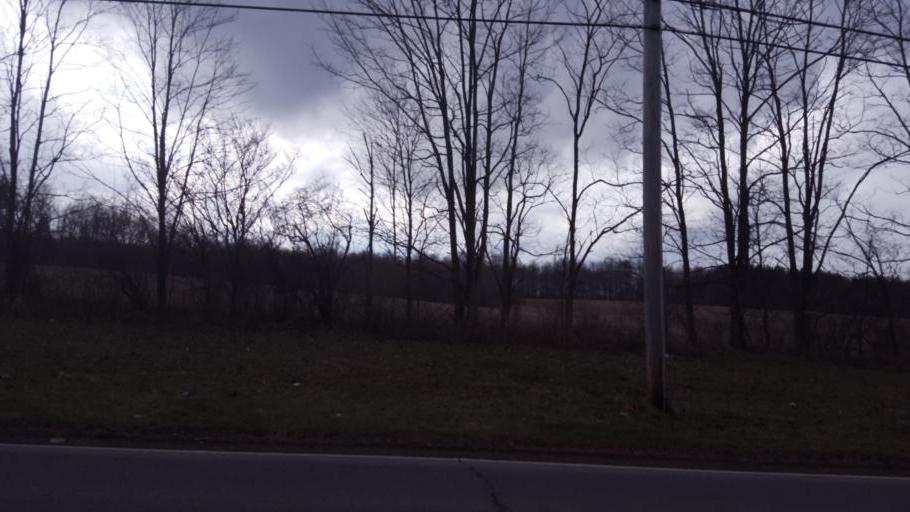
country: US
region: Ohio
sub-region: Richland County
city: Ontario
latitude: 40.8062
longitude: -82.5902
